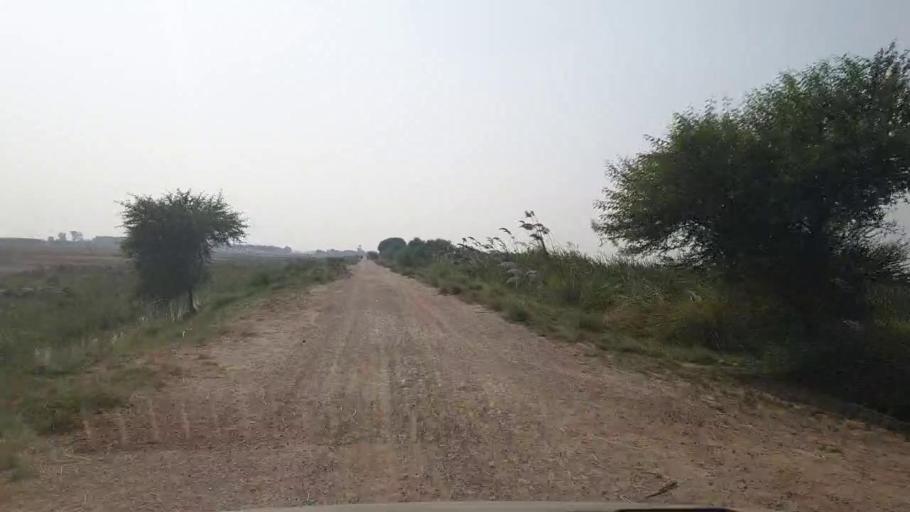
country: PK
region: Sindh
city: Bulri
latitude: 25.0263
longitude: 68.3918
